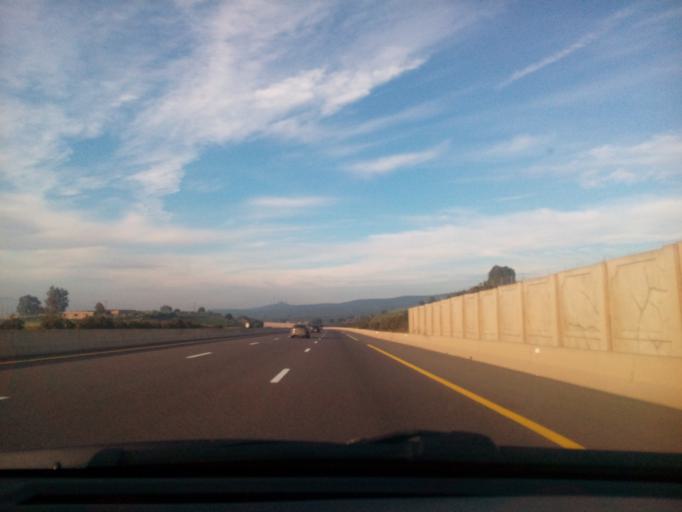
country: DZ
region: Relizane
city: Relizane
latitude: 35.7149
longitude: 0.2778
